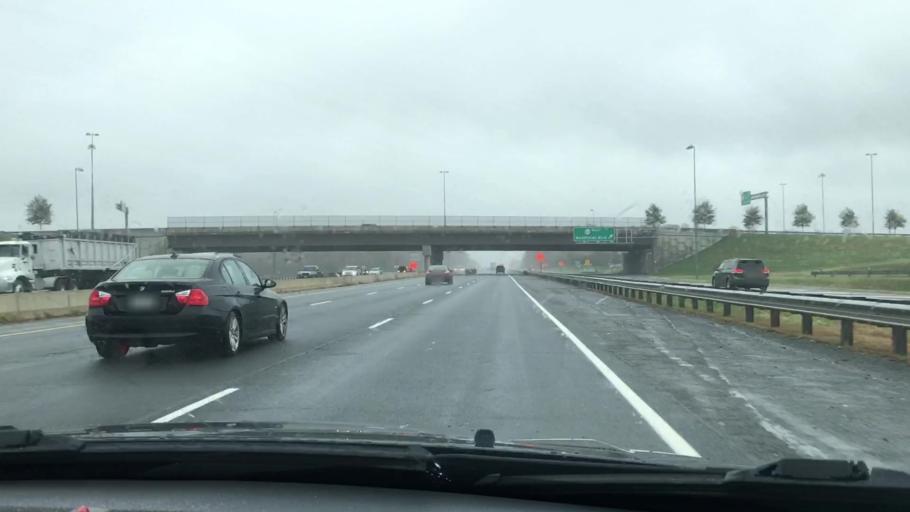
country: US
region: Virginia
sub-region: Fairfax County
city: Chantilly
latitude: 38.8743
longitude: -77.4464
